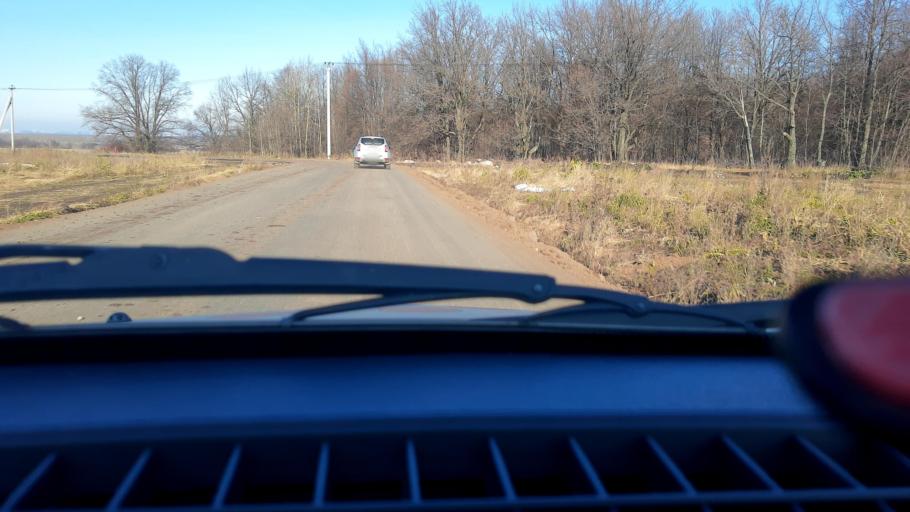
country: RU
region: Bashkortostan
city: Kabakovo
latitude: 54.6213
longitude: 56.1539
